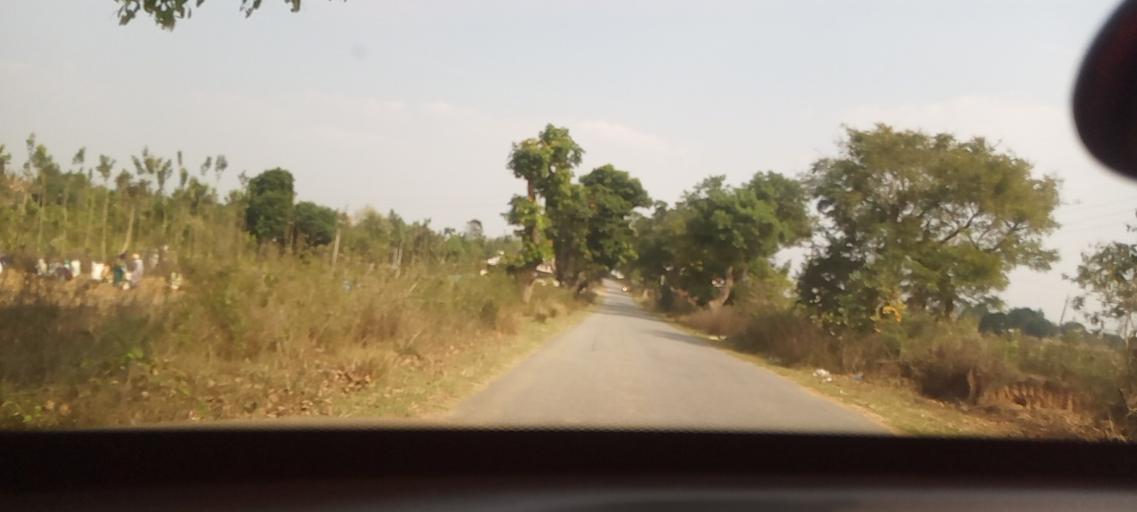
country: IN
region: Karnataka
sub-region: Hassan
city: Belur
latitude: 13.1760
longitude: 75.8497
